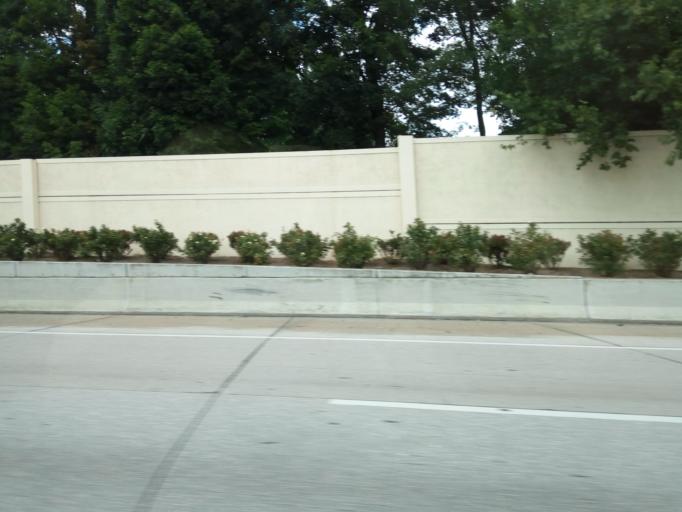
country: US
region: Kentucky
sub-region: Jefferson County
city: West Buechel
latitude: 38.2073
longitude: -85.6777
